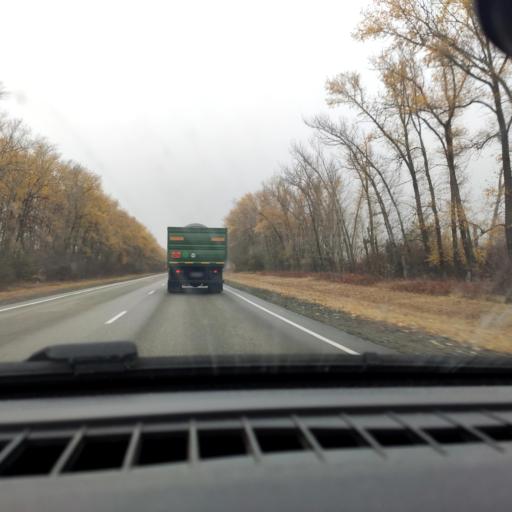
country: RU
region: Voronezj
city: Ostrogozhsk
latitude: 50.9818
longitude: 38.9949
